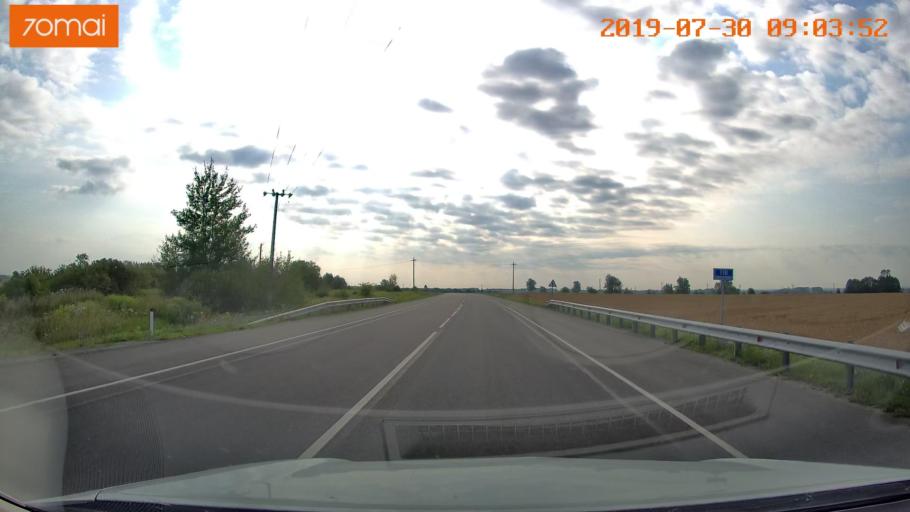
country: RU
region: Kaliningrad
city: Gusev
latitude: 54.6057
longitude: 22.2647
